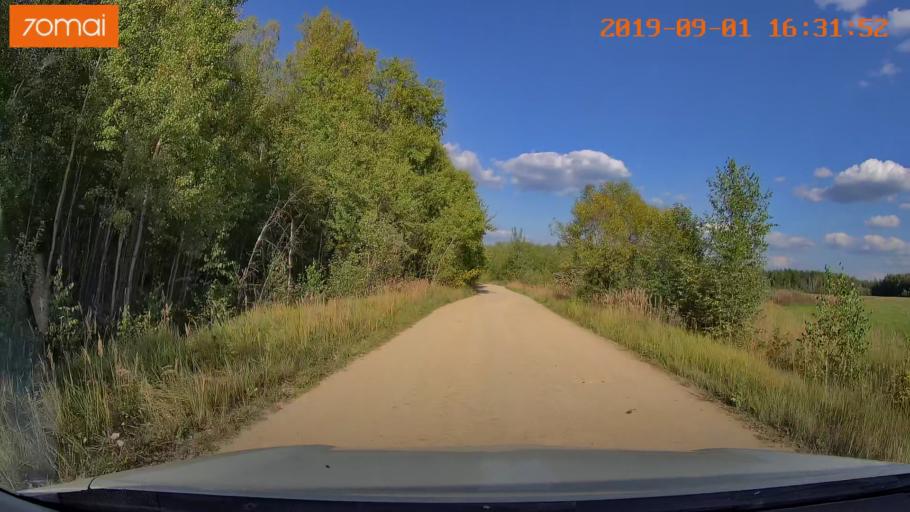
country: RU
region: Kaluga
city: Maloyaroslavets
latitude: 54.9498
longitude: 36.4661
